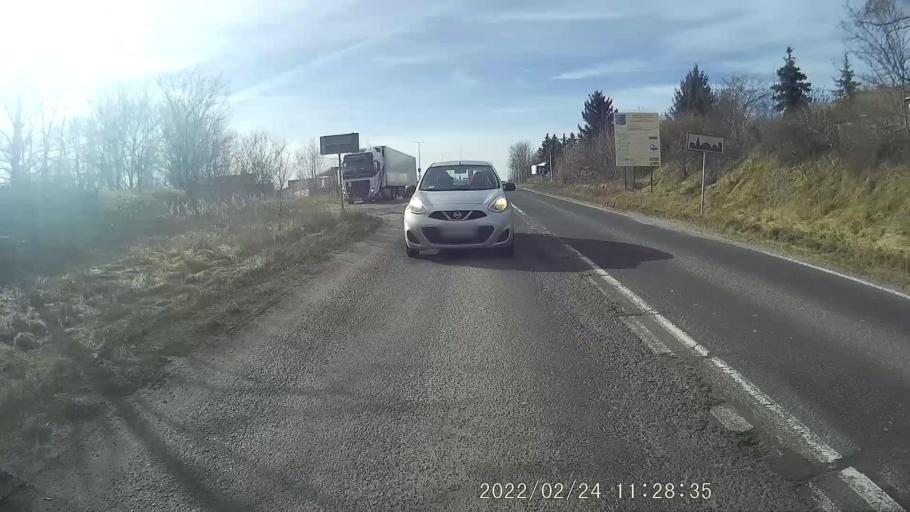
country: PL
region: Lower Silesian Voivodeship
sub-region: Powiat polkowicki
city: Przemkow
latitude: 51.5316
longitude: 15.6875
